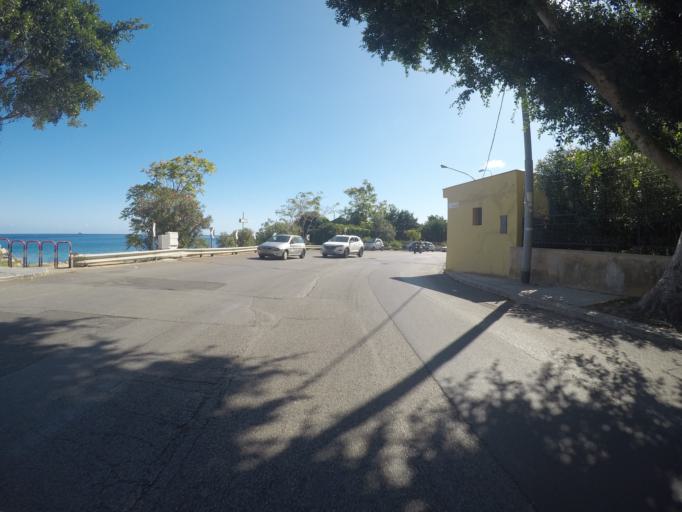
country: IT
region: Sicily
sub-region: Palermo
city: Palermo
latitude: 38.1654
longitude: 13.3687
